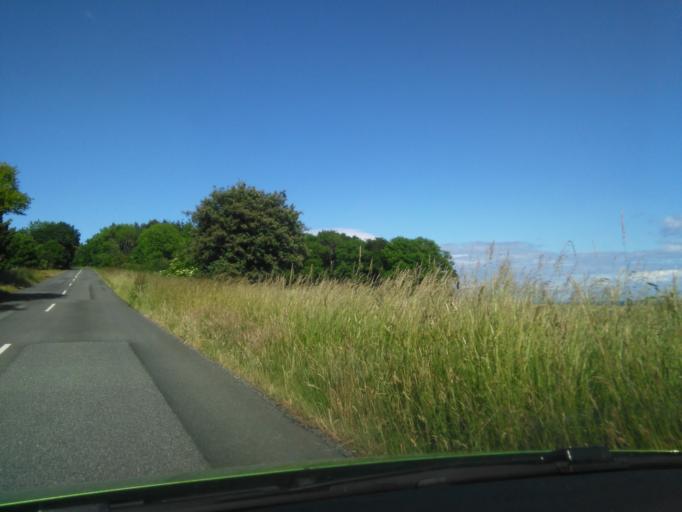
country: DK
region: Capital Region
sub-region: Bornholm Kommune
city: Nexo
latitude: 55.0647
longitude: 15.0795
